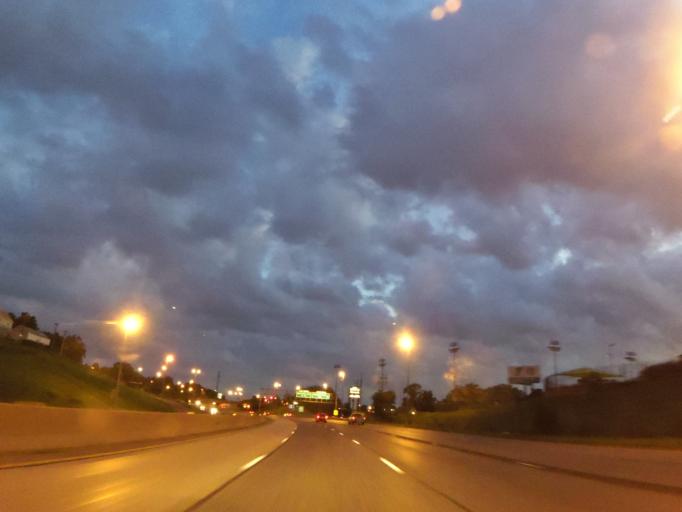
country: US
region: Missouri
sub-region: Saint Louis County
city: Lemay
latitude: 38.5593
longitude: -90.2568
